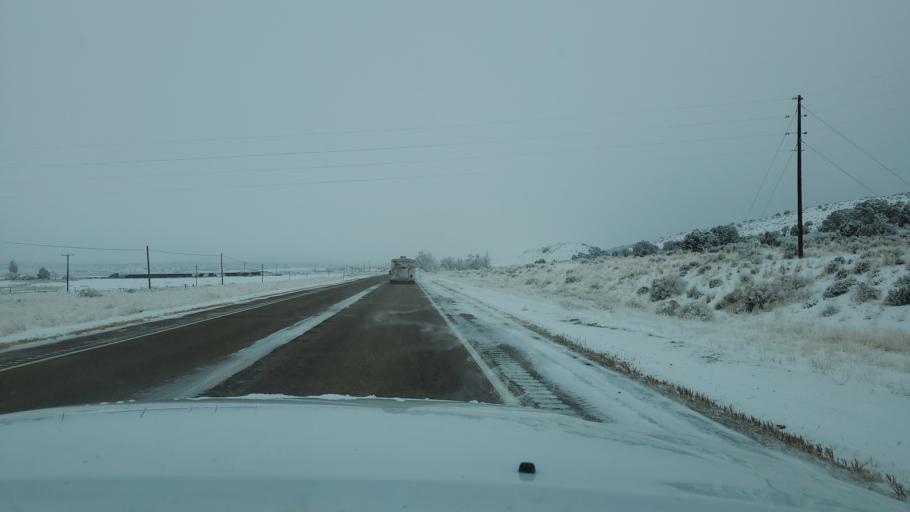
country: US
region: Colorado
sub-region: Rio Blanco County
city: Rangely
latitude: 40.2433
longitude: -108.9868
